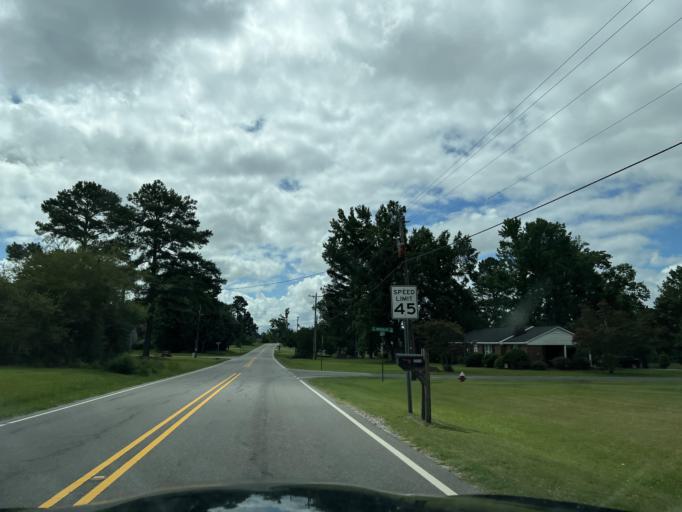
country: US
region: North Carolina
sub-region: Lee County
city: Sanford
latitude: 35.4339
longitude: -79.1648
